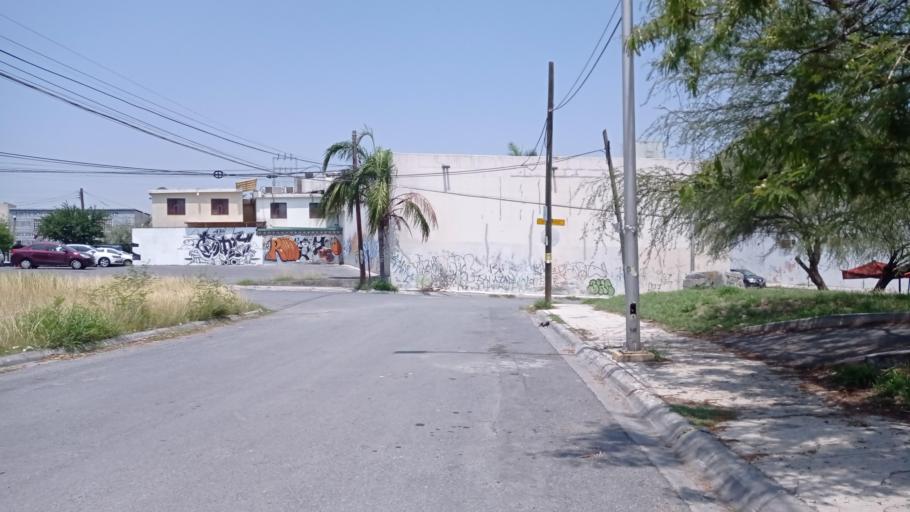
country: MX
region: Nuevo Leon
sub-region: Juarez
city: Jardines de la Silla (Jardines)
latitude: 25.6558
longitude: -100.1903
